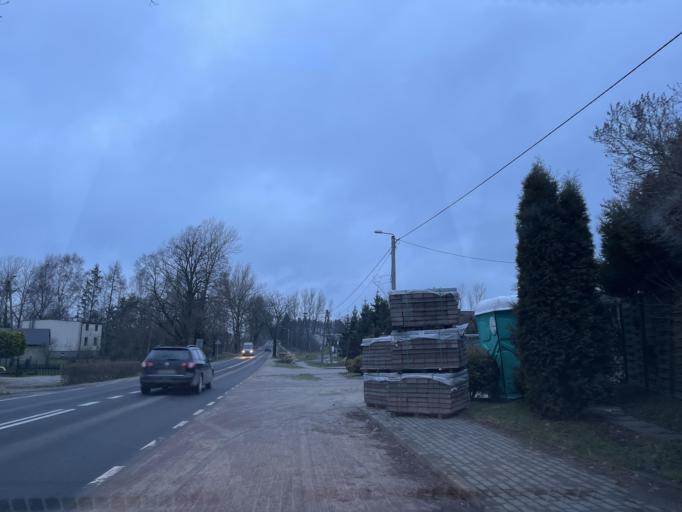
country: PL
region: Pomeranian Voivodeship
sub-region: Powiat wejherowski
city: Szemud
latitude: 54.4359
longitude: 18.1708
